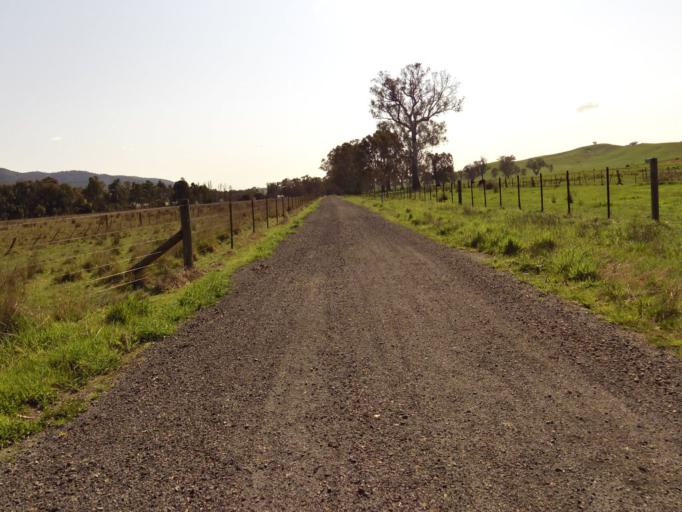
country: AU
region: Victoria
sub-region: Murrindindi
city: Alexandra
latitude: -37.1476
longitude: 145.5876
